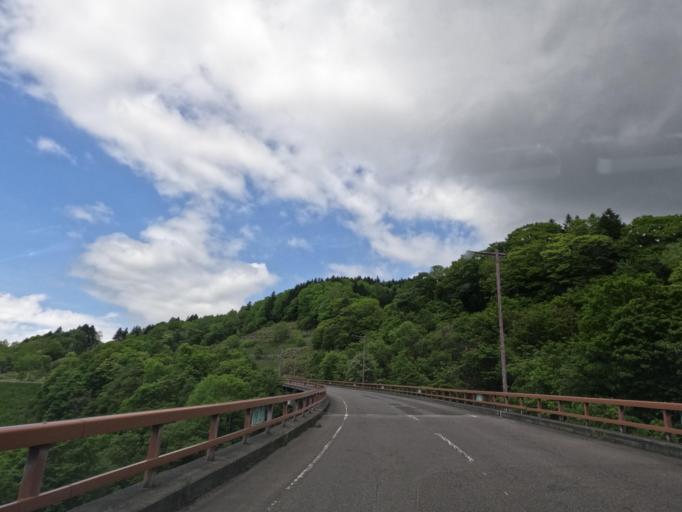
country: JP
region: Hokkaido
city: Tobetsu
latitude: 43.4761
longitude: 141.5963
